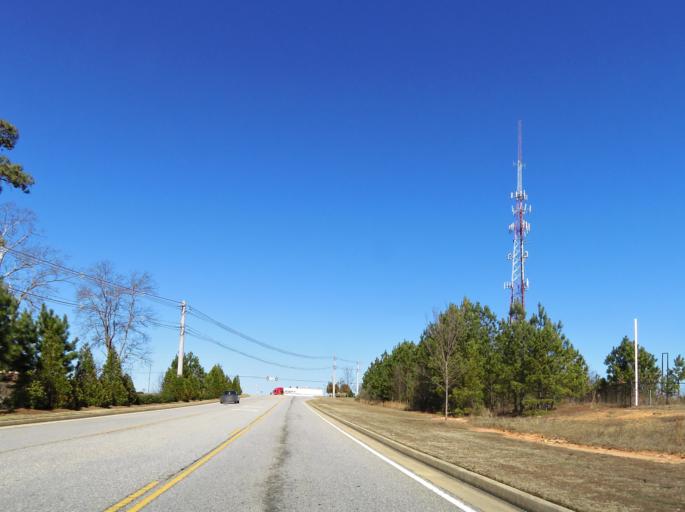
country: US
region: Georgia
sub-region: Peach County
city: Byron
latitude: 32.7421
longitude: -83.7225
